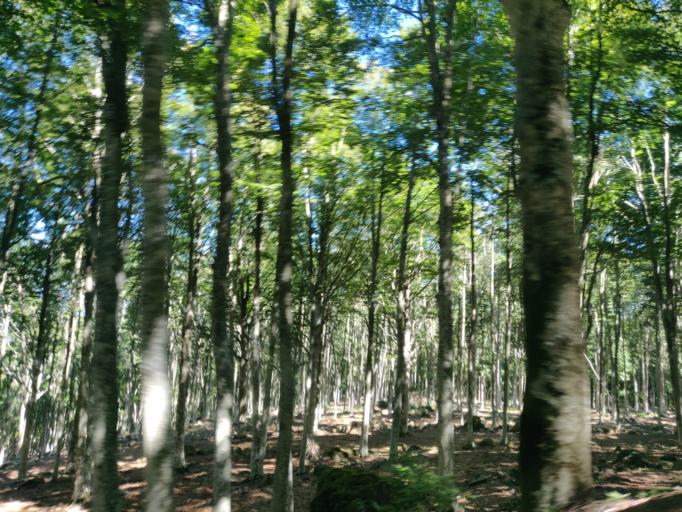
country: IT
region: Tuscany
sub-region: Provincia di Siena
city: Abbadia San Salvatore
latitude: 42.8993
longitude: 11.6316
